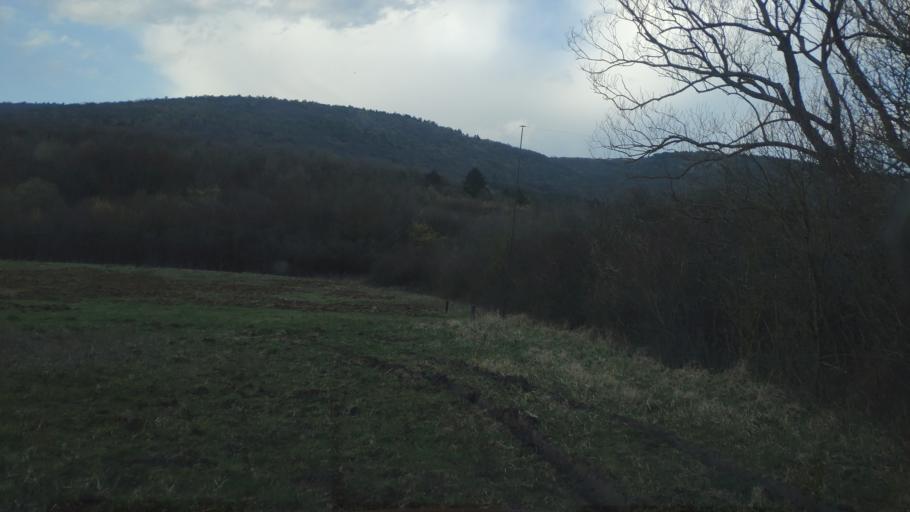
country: SK
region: Kosicky
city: Moldava nad Bodvou
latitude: 48.6158
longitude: 20.9175
